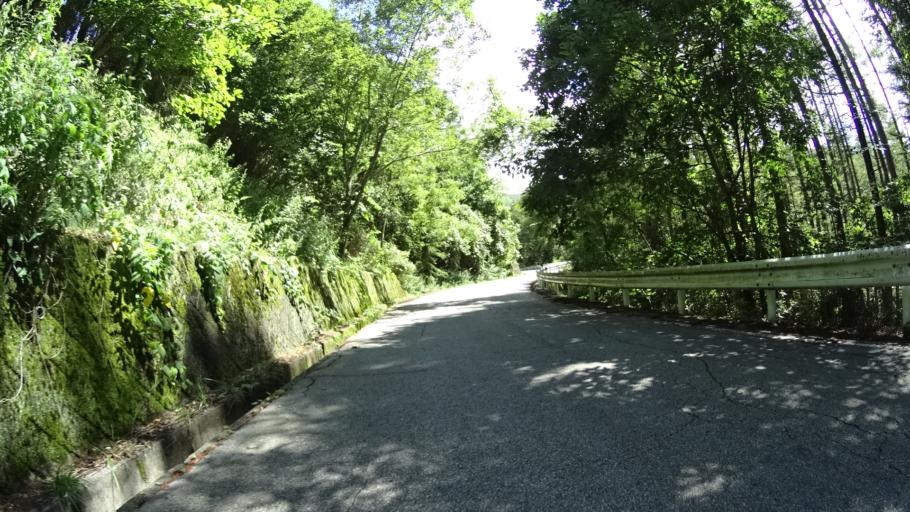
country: JP
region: Yamanashi
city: Enzan
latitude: 35.7223
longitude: 138.8412
